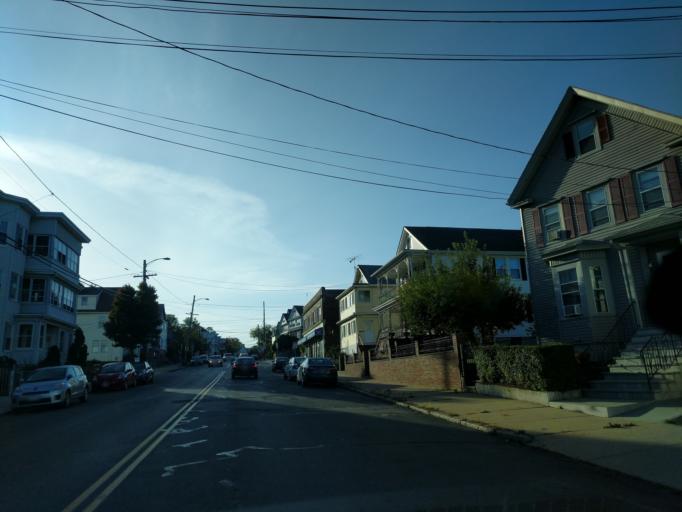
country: US
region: Massachusetts
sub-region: Middlesex County
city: Somerville
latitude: 42.3979
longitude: -71.1005
